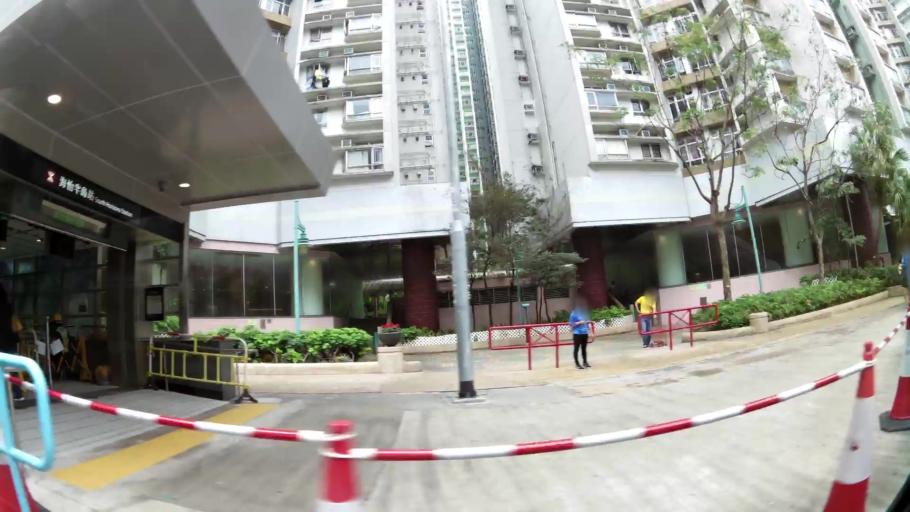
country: HK
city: Yung Shue Wan
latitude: 22.2429
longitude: 114.1481
